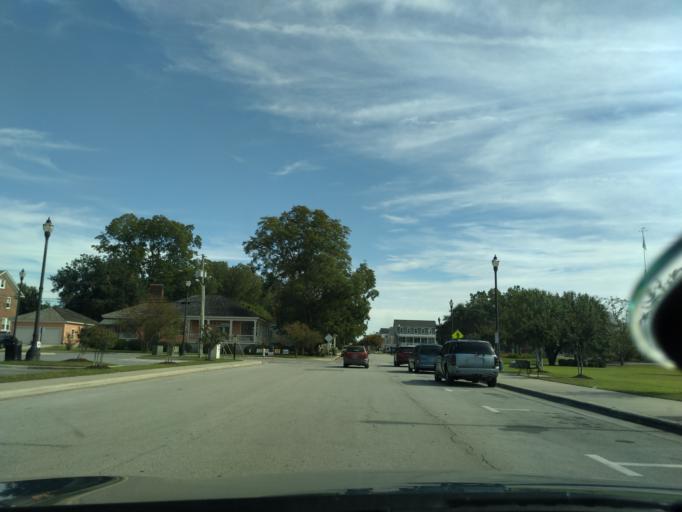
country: US
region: North Carolina
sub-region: Beaufort County
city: Washington
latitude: 35.5410
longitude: -77.0548
